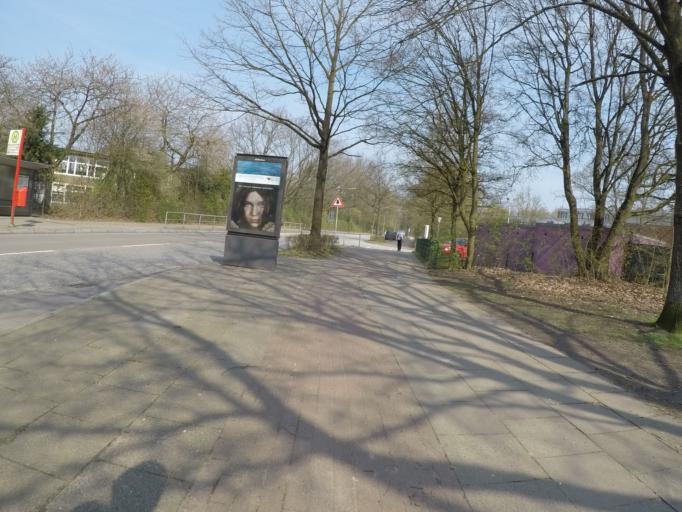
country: DE
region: Hamburg
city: Hummelsbuettel
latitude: 53.6447
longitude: 10.0518
